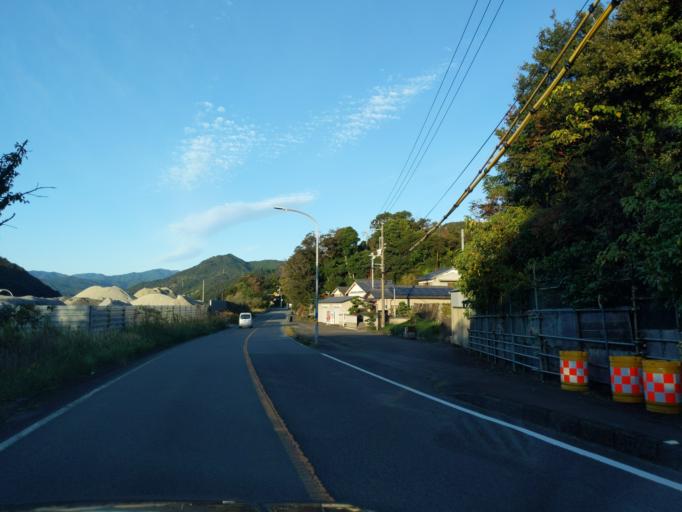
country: JP
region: Kochi
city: Muroto-misakicho
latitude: 33.5854
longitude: 134.3462
